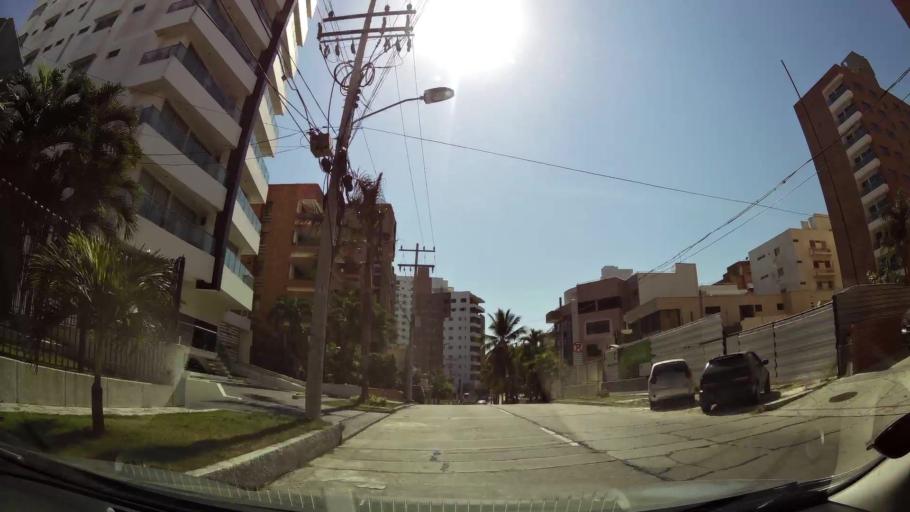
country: CO
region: Atlantico
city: Barranquilla
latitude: 11.0152
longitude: -74.8199
